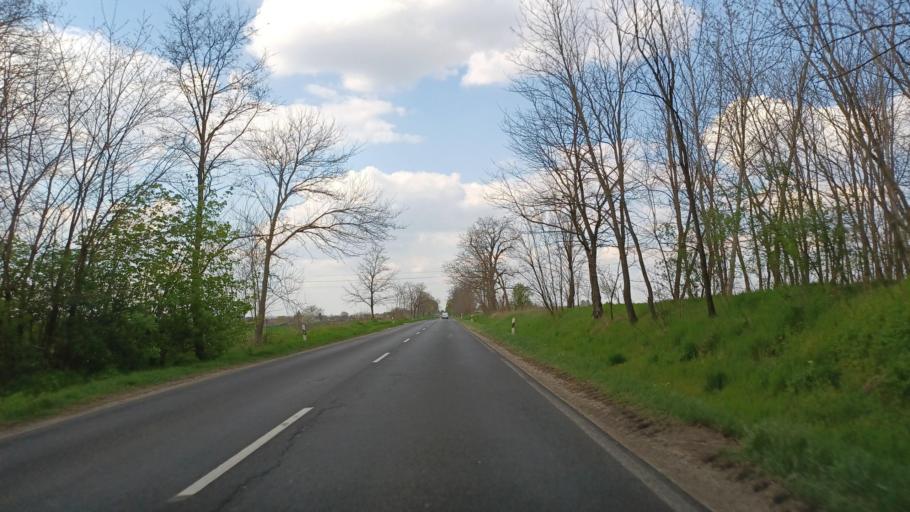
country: HU
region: Fejer
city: Cece
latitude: 46.7492
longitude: 18.6435
